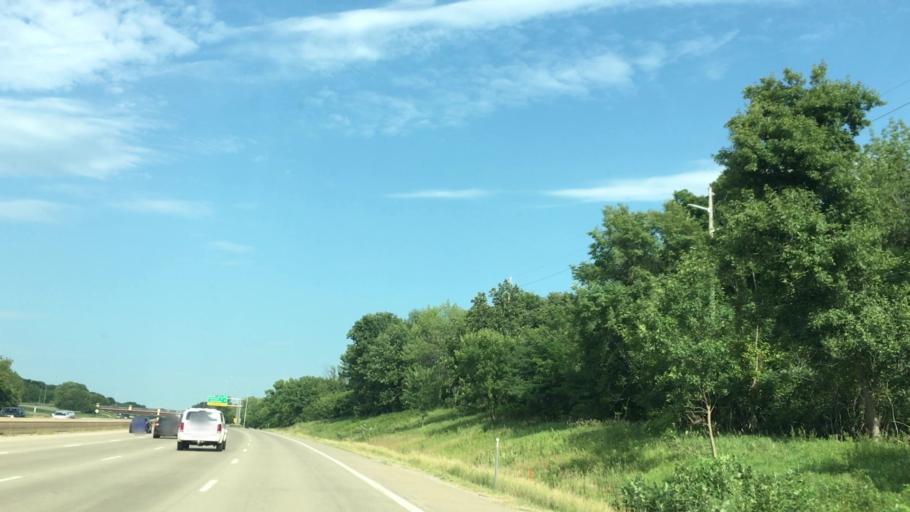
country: US
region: Iowa
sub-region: Johnson County
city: Iowa City
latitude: 41.6853
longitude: -91.5475
